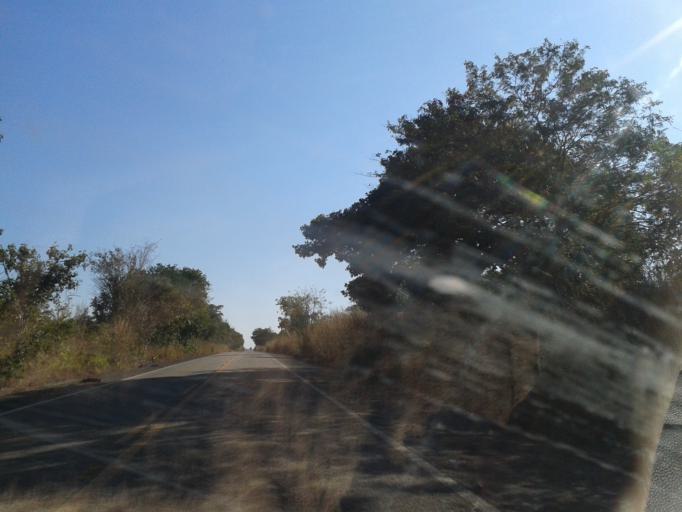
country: BR
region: Goias
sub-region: Mozarlandia
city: Mozarlandia
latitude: -14.9776
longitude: -50.5808
